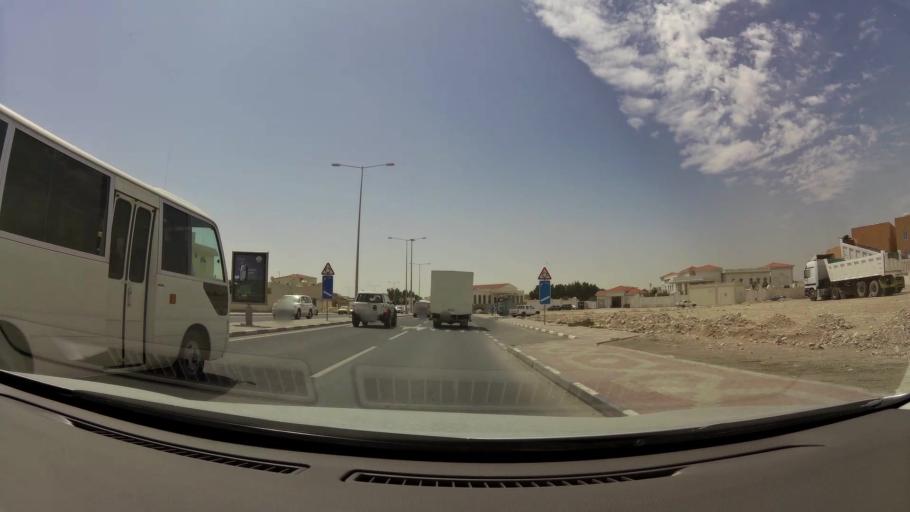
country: QA
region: Baladiyat ar Rayyan
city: Ar Rayyan
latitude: 25.2615
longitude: 51.4197
